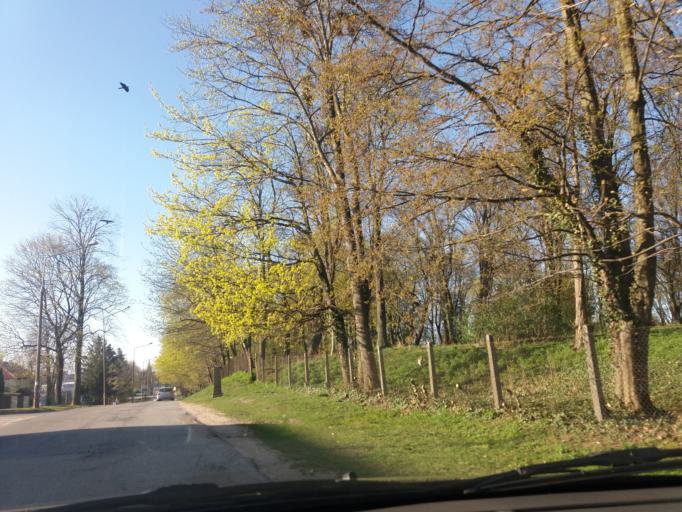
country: PL
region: Warmian-Masurian Voivodeship
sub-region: Powiat nidzicki
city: Nidzica
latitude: 53.3500
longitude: 20.4298
